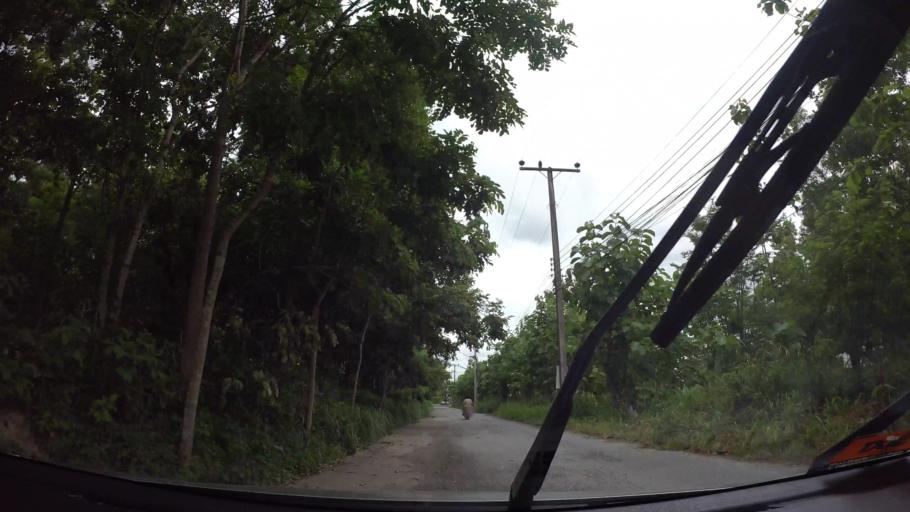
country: TH
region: Chon Buri
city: Si Racha
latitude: 13.1618
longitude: 100.9786
